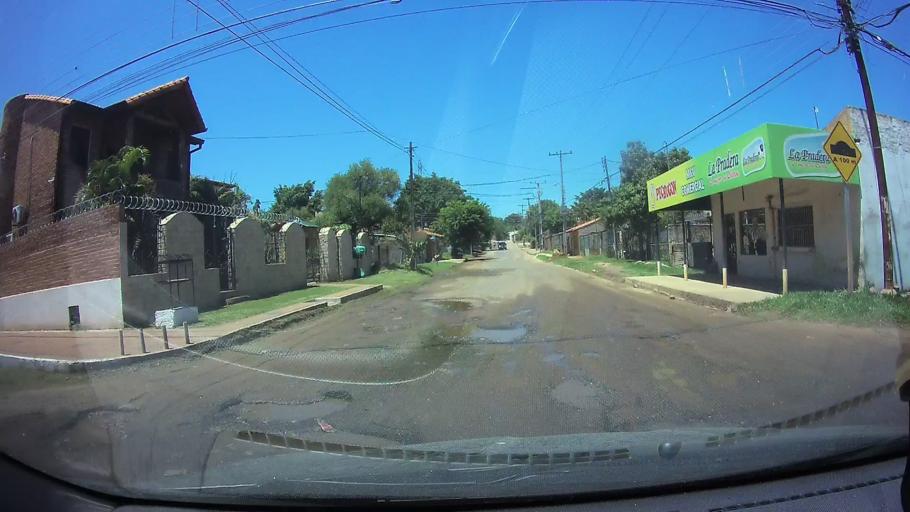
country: PY
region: Central
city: San Lorenzo
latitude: -25.3279
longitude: -57.4855
